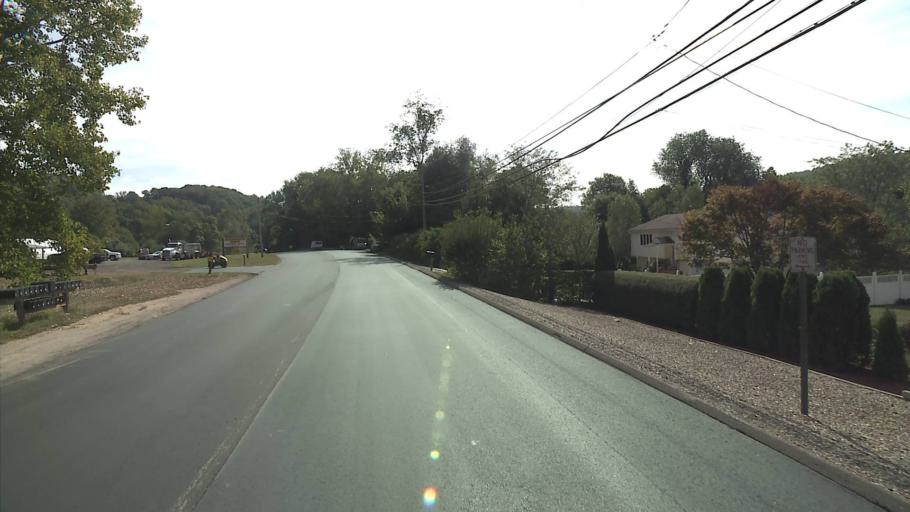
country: US
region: Connecticut
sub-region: Fairfield County
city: Shelton
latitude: 41.3415
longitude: -73.1204
